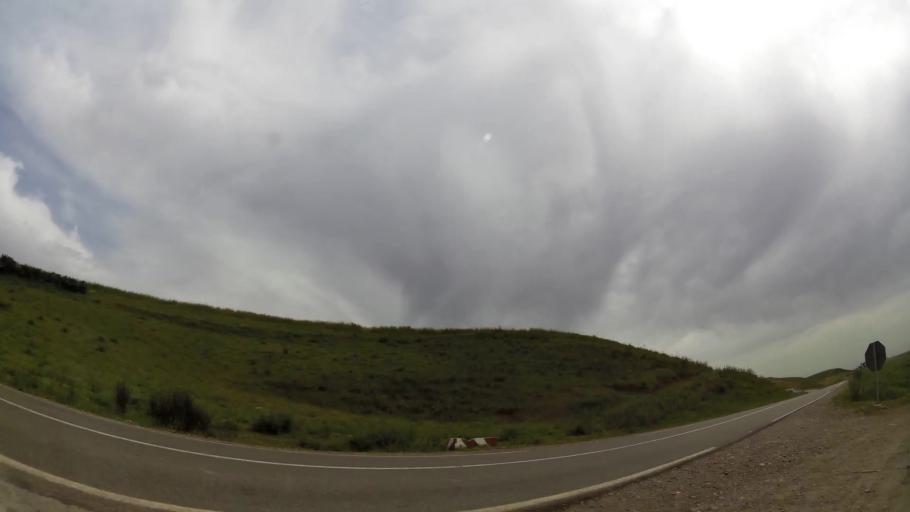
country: MA
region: Rabat-Sale-Zemmour-Zaer
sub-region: Khemisset
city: Khemisset
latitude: 33.7585
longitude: -6.2114
